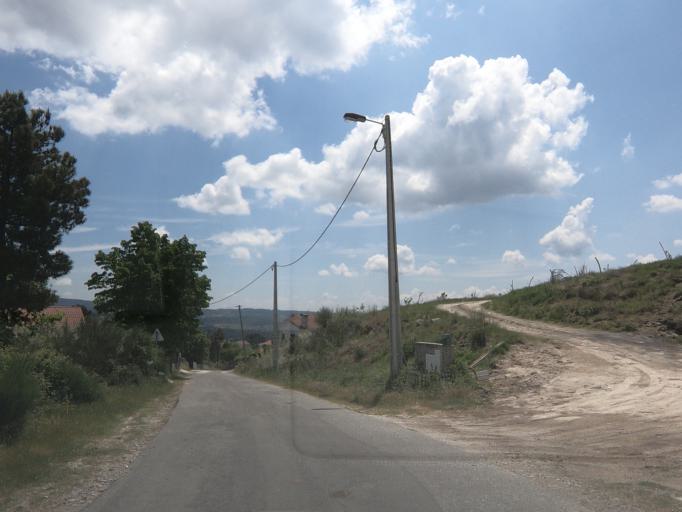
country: PT
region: Vila Real
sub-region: Vila Real
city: Vila Real
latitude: 41.3538
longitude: -7.7298
